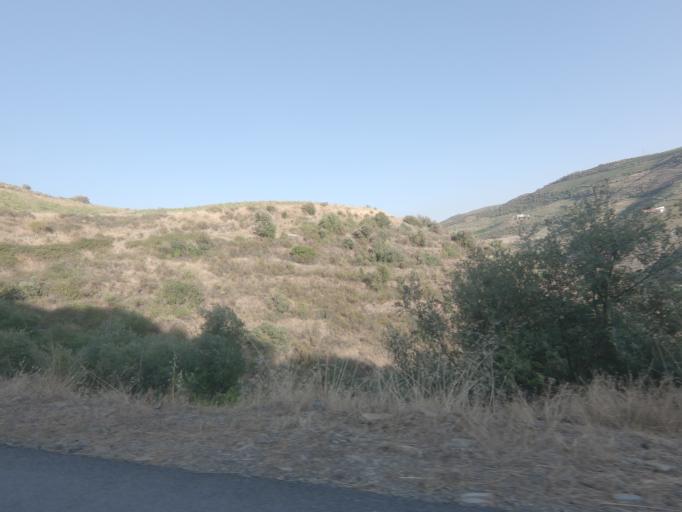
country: PT
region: Viseu
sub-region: Tabuaco
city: Tabuaco
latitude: 41.1621
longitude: -7.6041
